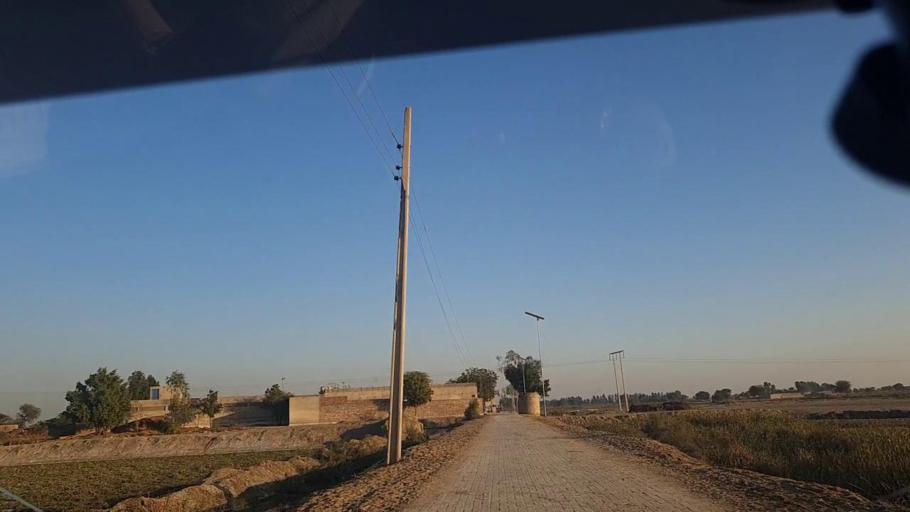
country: PK
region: Sindh
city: Khanpur
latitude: 27.8659
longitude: 69.4247
